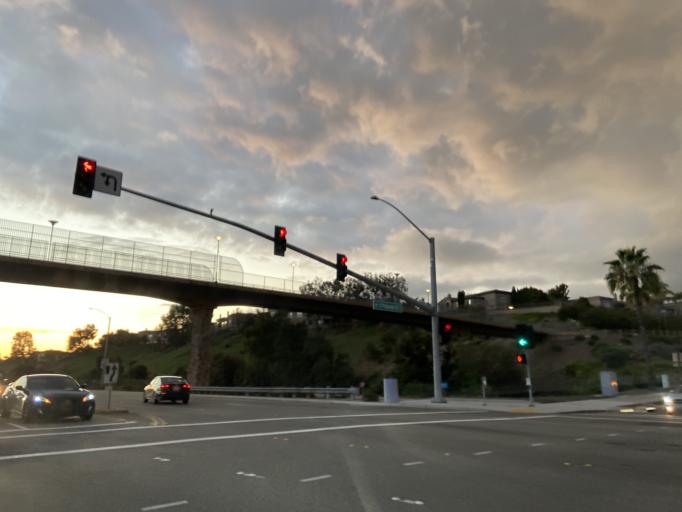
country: US
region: California
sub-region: San Diego County
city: Bonita
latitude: 32.6296
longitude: -116.9794
